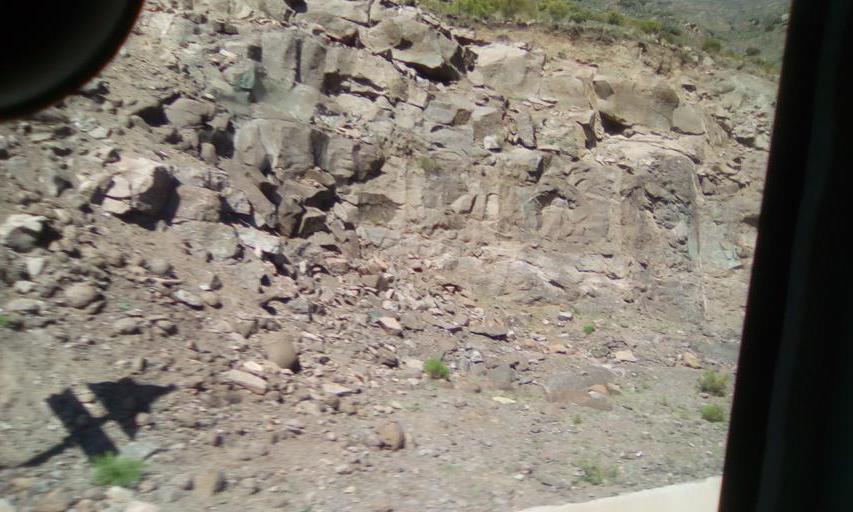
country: LS
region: Qacha's Nek
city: Qacha's Nek
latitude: -30.0100
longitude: 28.1652
